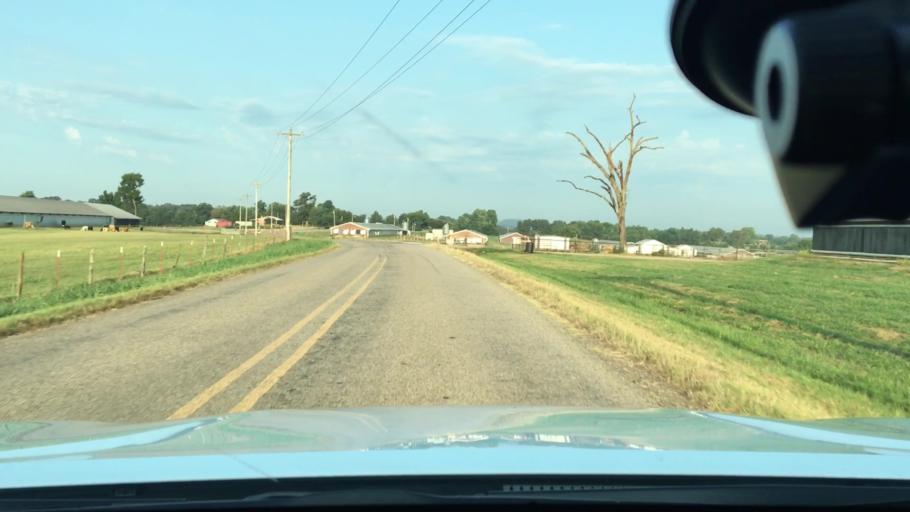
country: US
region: Arkansas
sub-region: Johnson County
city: Coal Hill
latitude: 35.3728
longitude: -93.5733
